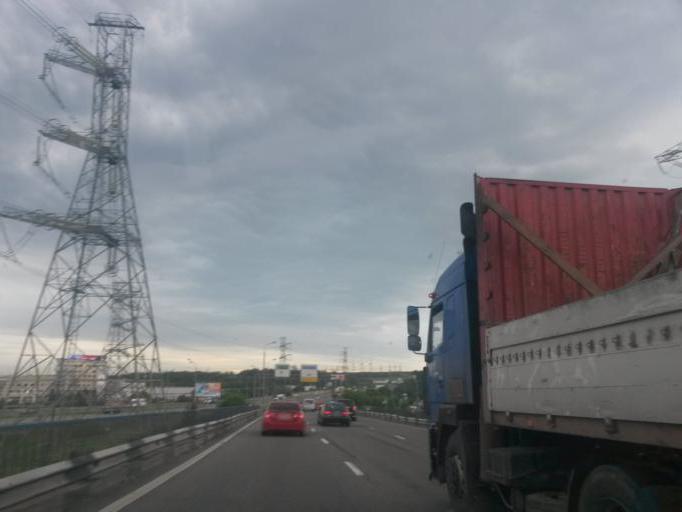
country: RU
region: Moscow
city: Annino
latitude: 55.5709
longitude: 37.5969
